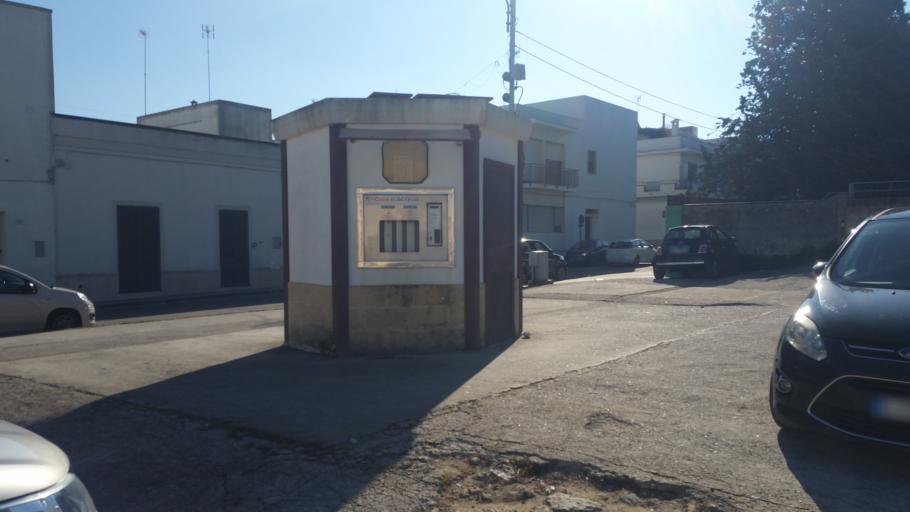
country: IT
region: Apulia
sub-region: Provincia di Lecce
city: Tricase
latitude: 39.9252
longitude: 18.3626
